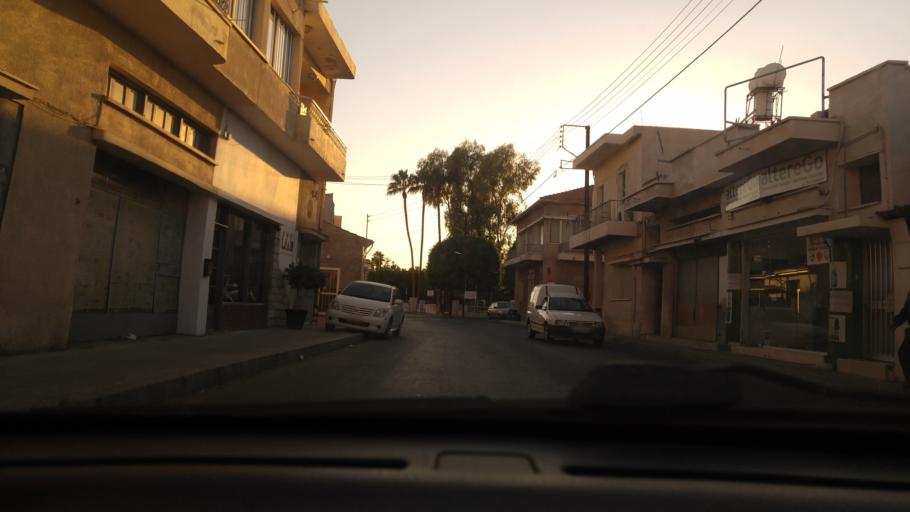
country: CY
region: Limassol
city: Limassol
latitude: 34.6747
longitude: 33.0354
